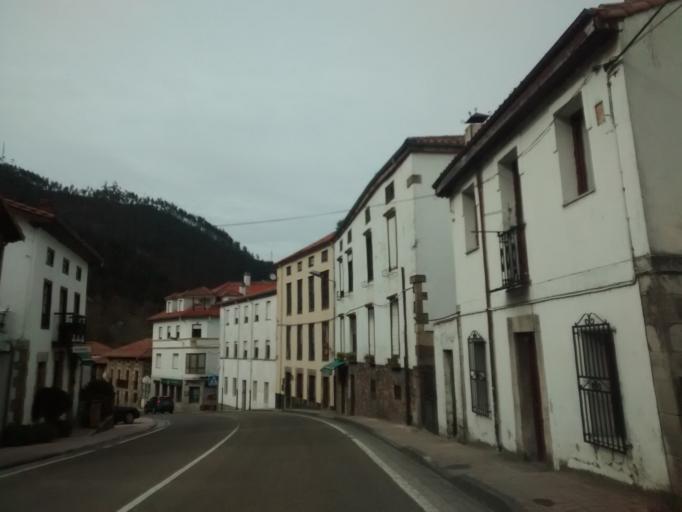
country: ES
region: Cantabria
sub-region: Provincia de Cantabria
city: Puente Viesgo
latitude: 43.2980
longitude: -3.9667
